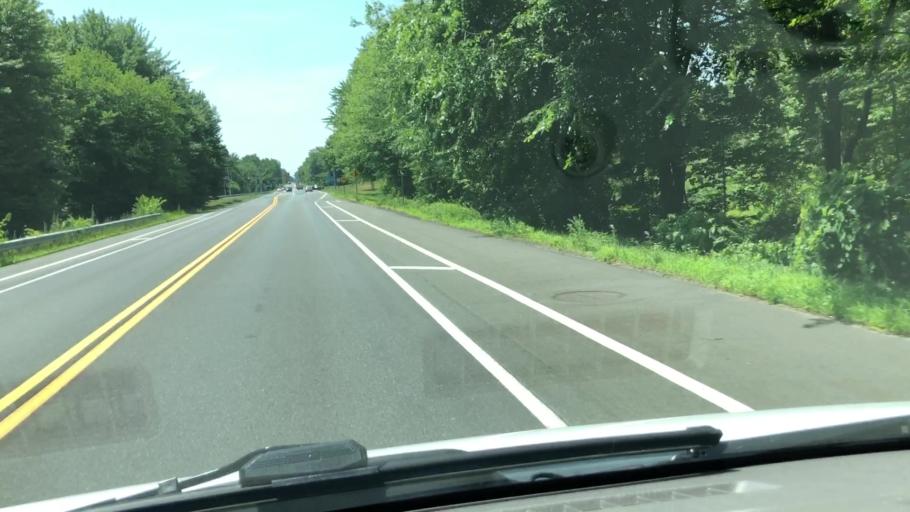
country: US
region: Massachusetts
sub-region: Franklin County
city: South Deerfield
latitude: 42.4850
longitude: -72.6122
